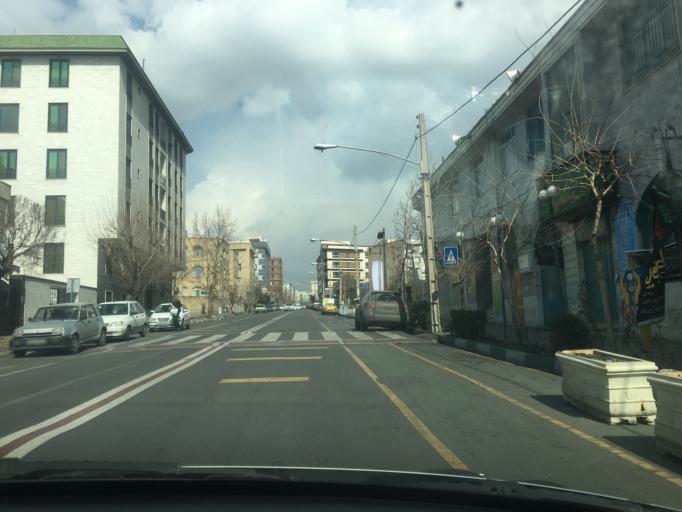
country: IR
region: Tehran
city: Tehran
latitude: 35.7190
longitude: 51.3226
